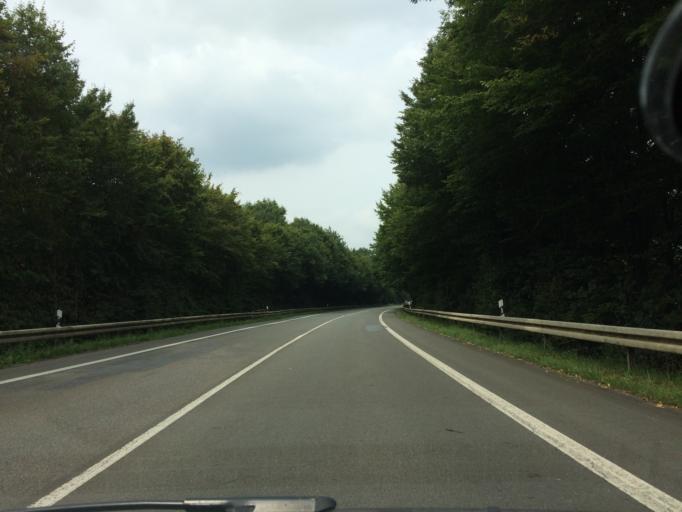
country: DE
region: North Rhine-Westphalia
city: Marl
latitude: 51.6932
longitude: 7.0670
